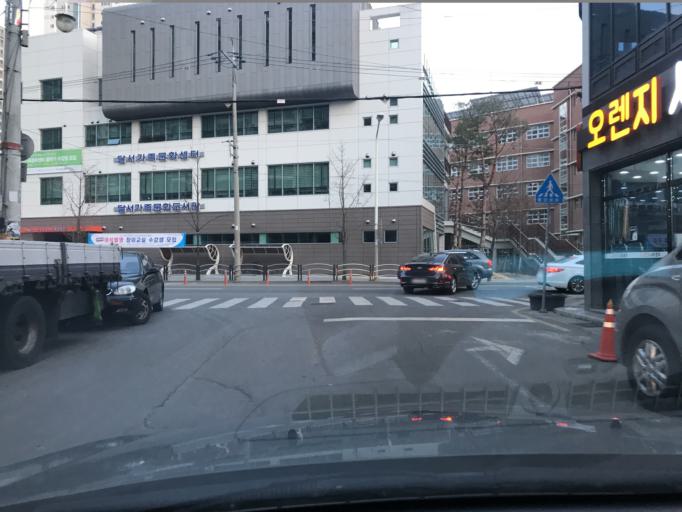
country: KR
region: Daegu
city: Hwawon
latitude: 35.8177
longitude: 128.5184
